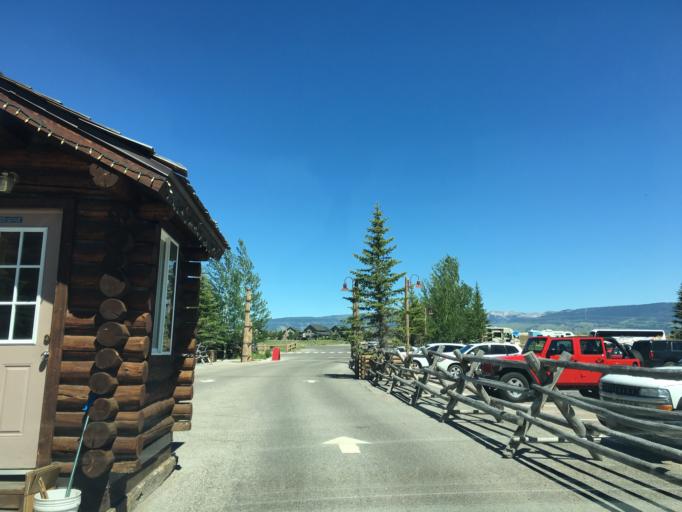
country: US
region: Wyoming
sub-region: Teton County
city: Moose Wilson Road
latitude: 43.5867
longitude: -110.8272
